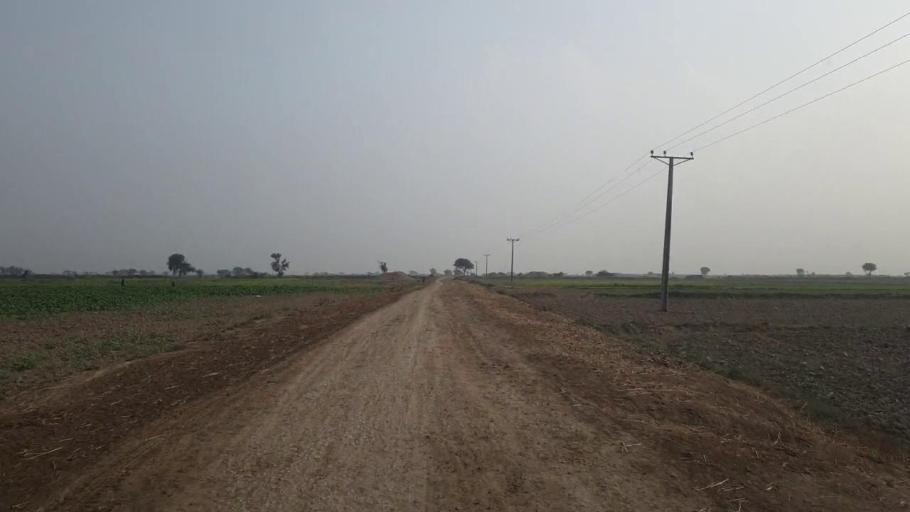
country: PK
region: Sindh
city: Mirpur Batoro
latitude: 24.5501
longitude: 68.4208
